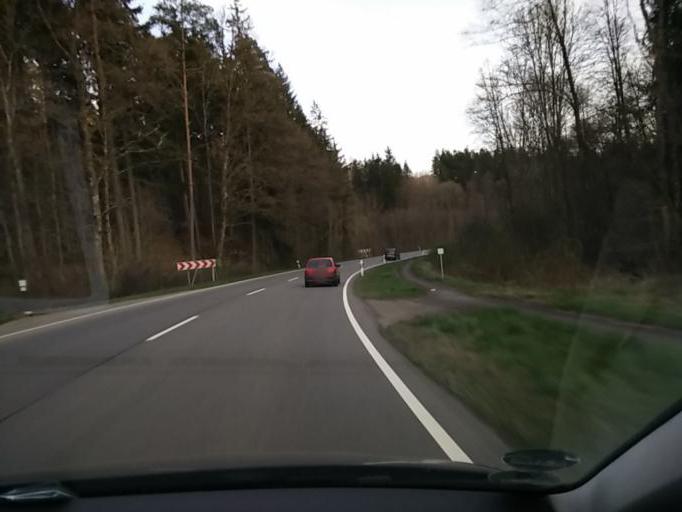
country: DE
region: Baden-Wuerttemberg
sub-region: Tuebingen Region
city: Dettenhausen
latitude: 48.5703
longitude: 9.0739
